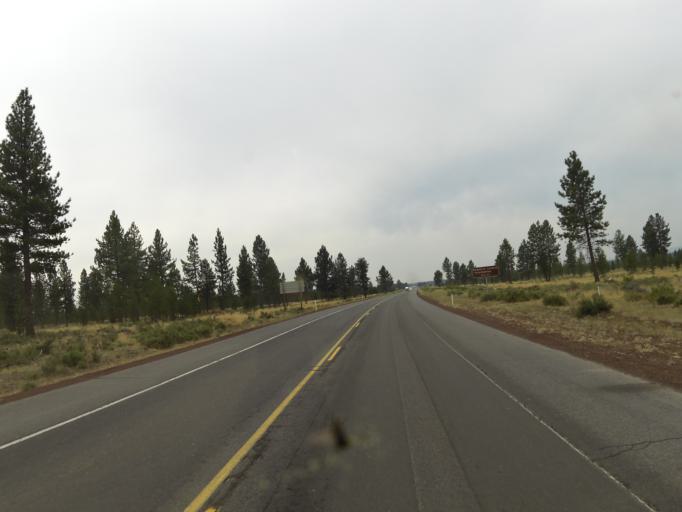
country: US
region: Oregon
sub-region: Deschutes County
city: Three Rivers
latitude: 43.7613
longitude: -121.4549
